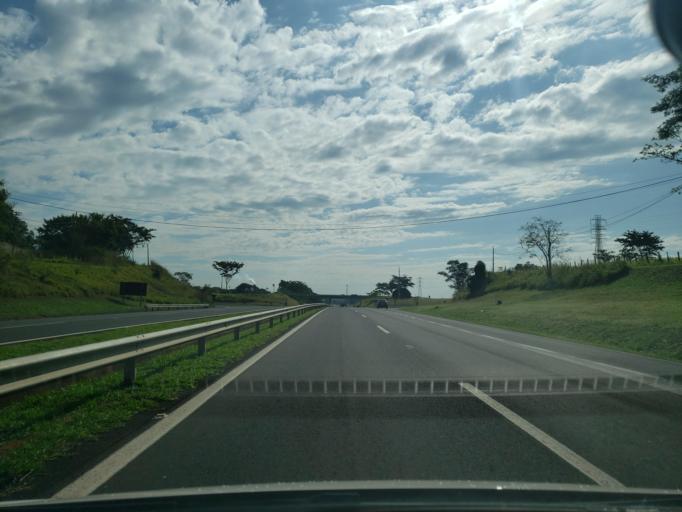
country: BR
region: Sao Paulo
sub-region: Lins
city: Lins
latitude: -21.6831
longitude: -49.7658
